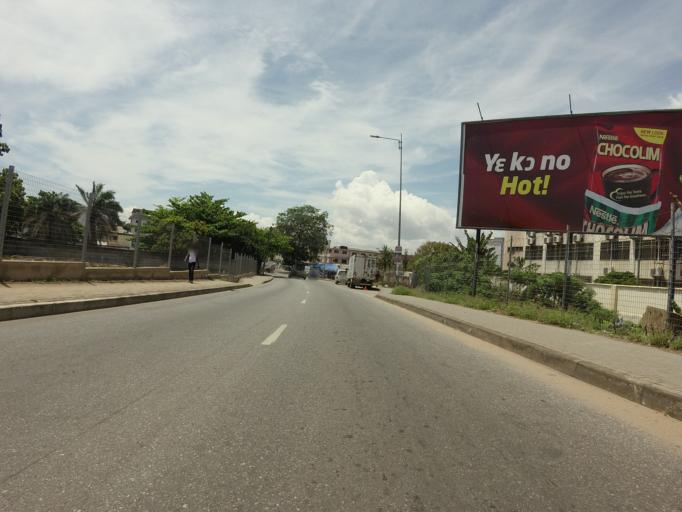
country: GH
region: Greater Accra
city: Accra
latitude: 5.5561
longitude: -0.2078
